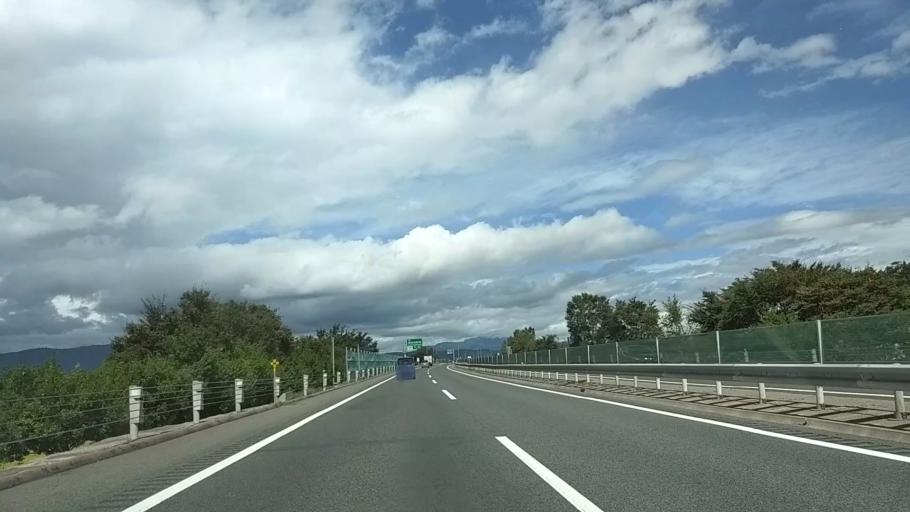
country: JP
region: Nagano
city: Suzaka
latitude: 36.6287
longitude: 138.2734
